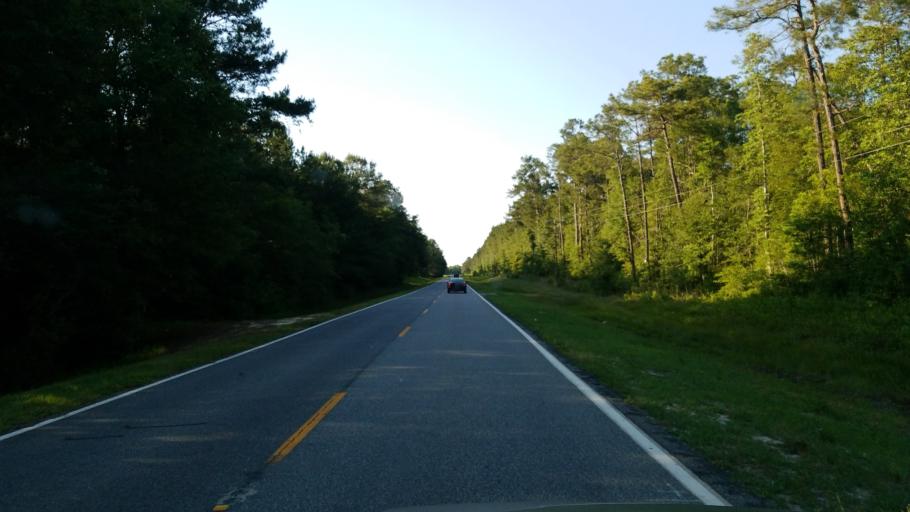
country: US
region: Georgia
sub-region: Lanier County
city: Lakeland
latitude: 30.9594
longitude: -83.0819
